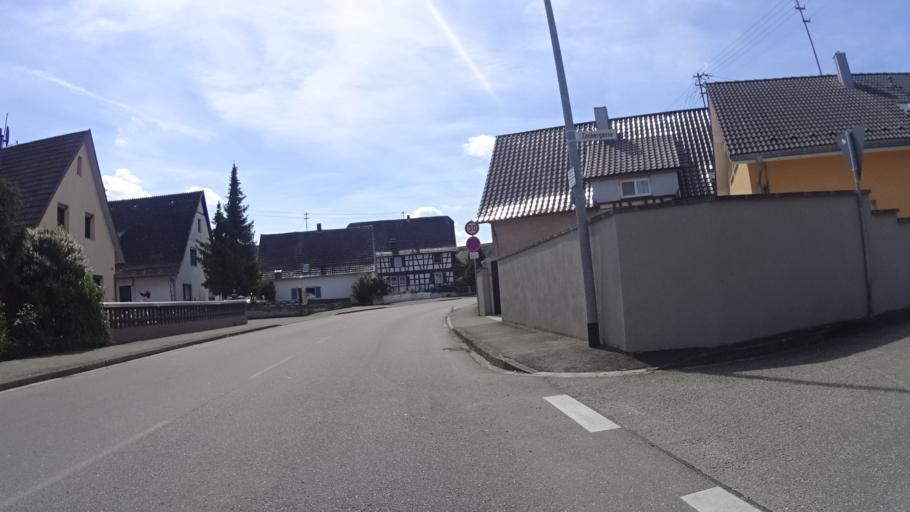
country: DE
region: Baden-Wuerttemberg
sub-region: Freiburg Region
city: Meissenheim
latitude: 48.4681
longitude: 7.8130
